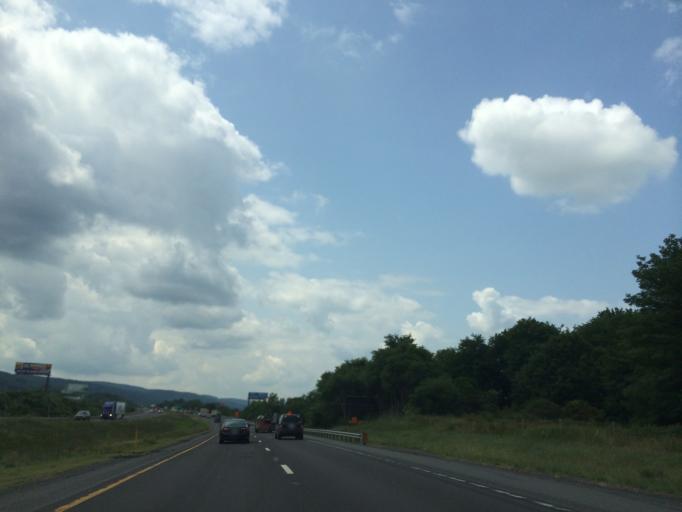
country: US
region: Pennsylvania
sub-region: Luzerne County
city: Georgetown
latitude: 41.2264
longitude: -75.8743
